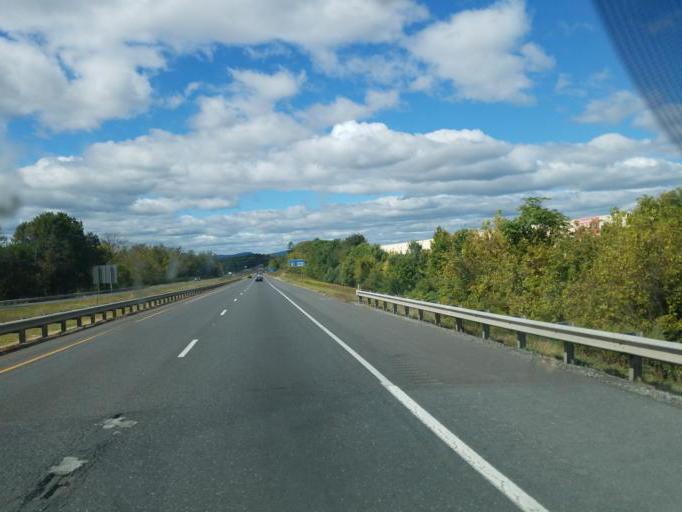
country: US
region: Maryland
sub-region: Washington County
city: Williamsport
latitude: 39.6251
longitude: -77.7972
